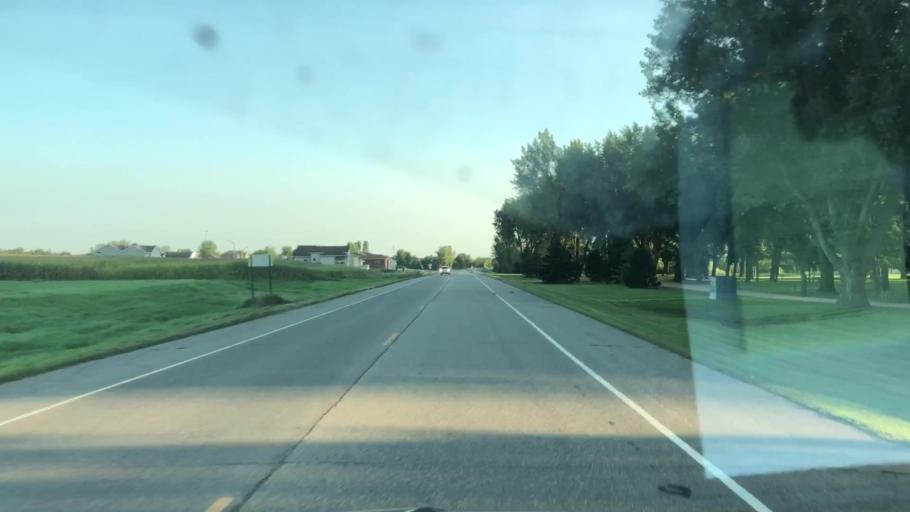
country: US
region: Minnesota
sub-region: Nobles County
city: Worthington
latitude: 43.6077
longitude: -95.6366
